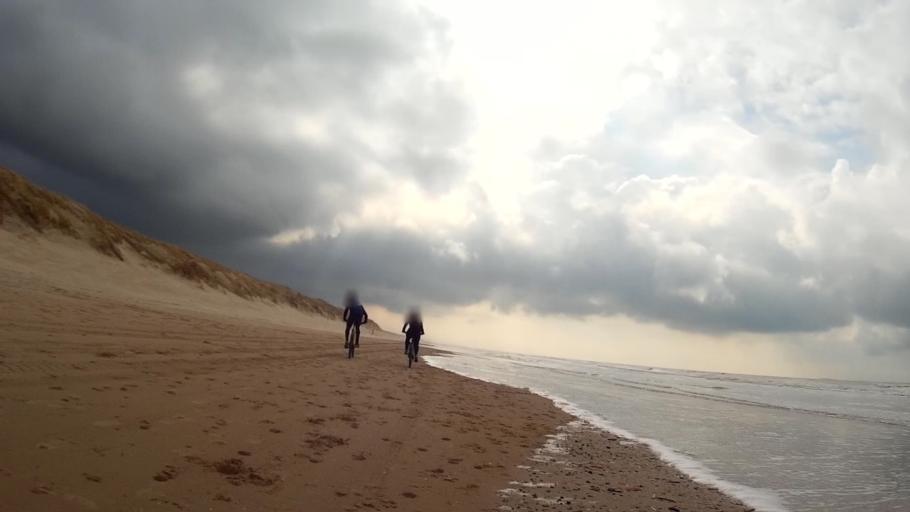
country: NL
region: North Holland
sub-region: Gemeente Bergen
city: Egmond aan Zee
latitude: 52.6961
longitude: 4.6349
